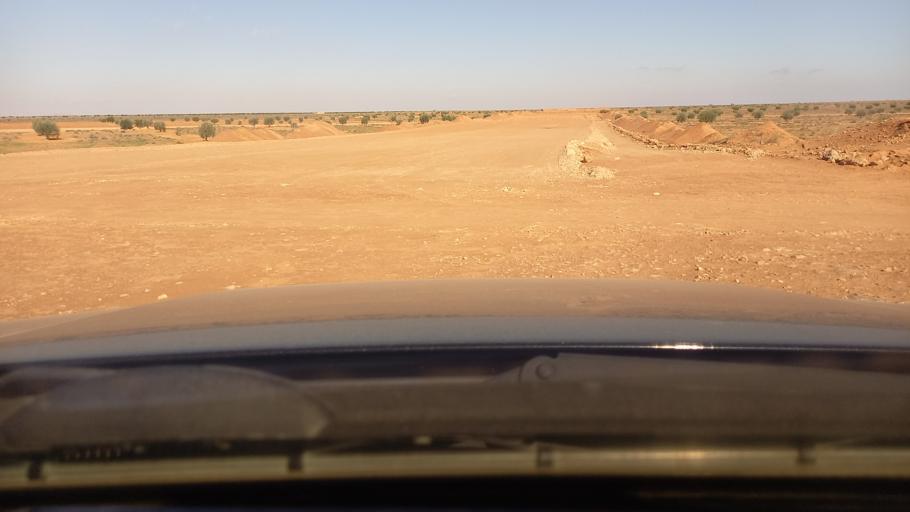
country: TN
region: Madanin
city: Medenine
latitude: 33.1755
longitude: 10.5282
